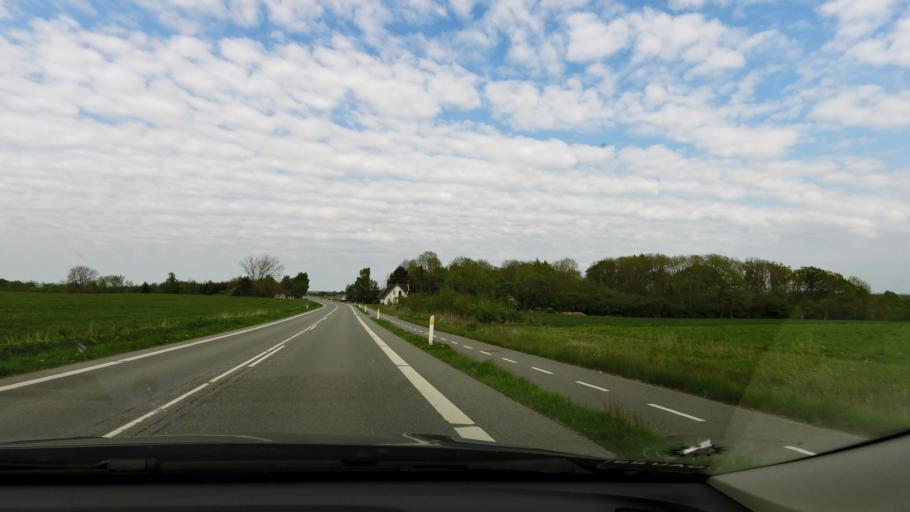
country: DK
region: South Denmark
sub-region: Nyborg Kommune
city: Nyborg
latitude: 55.2940
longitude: 10.7086
